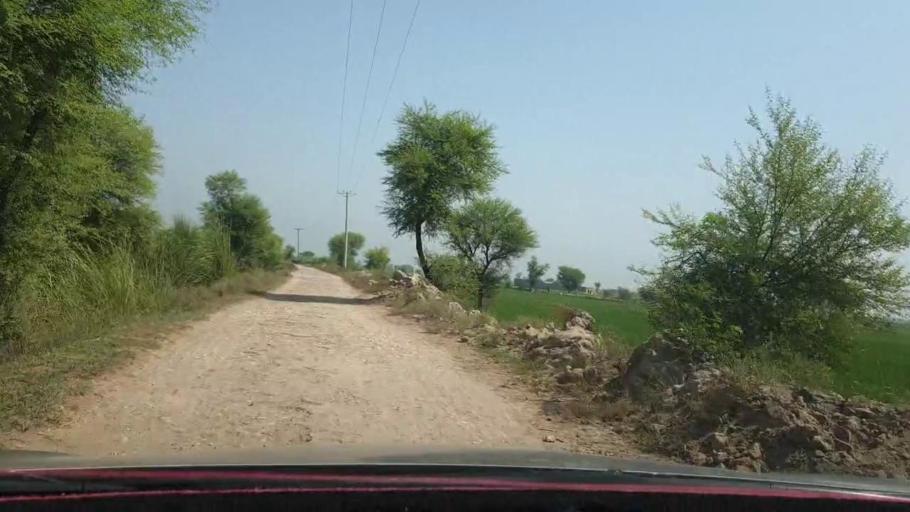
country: PK
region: Sindh
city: Warah
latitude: 27.4875
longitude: 67.8340
